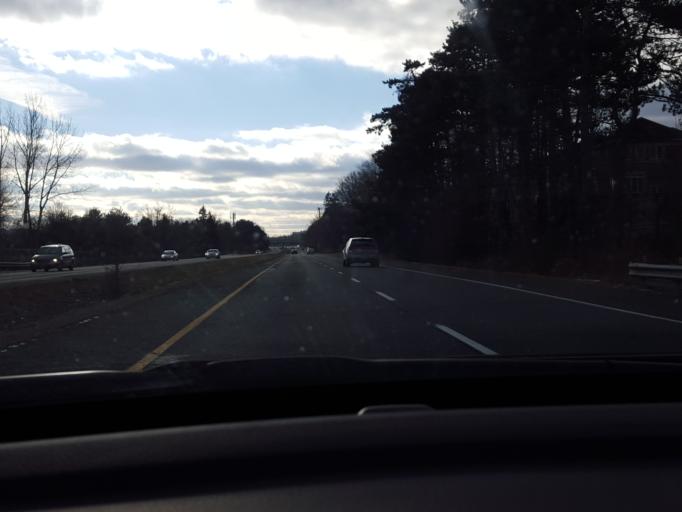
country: CA
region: Ontario
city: Scarborough
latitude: 43.7892
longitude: -79.1581
